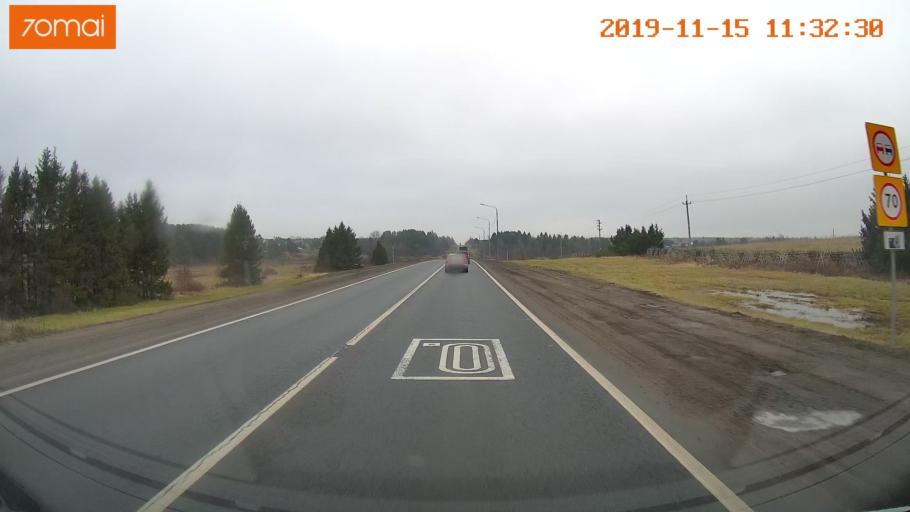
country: RU
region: Vologda
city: Molochnoye
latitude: 59.1858
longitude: 39.5753
